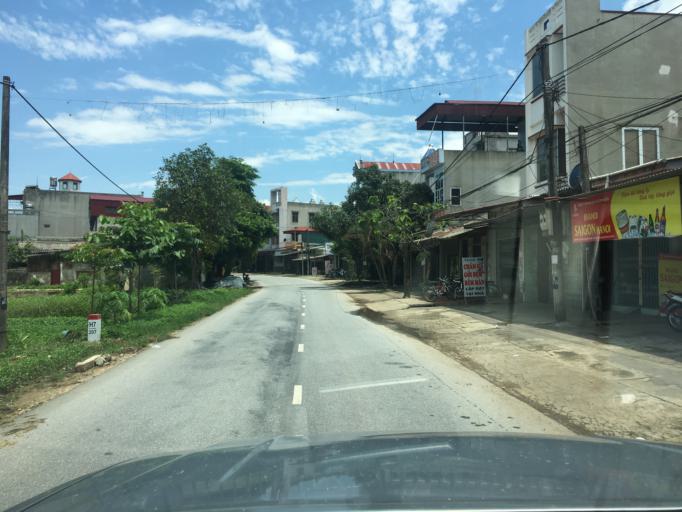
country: VN
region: Yen Bai
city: Son Thinh
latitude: 21.6408
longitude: 104.5010
